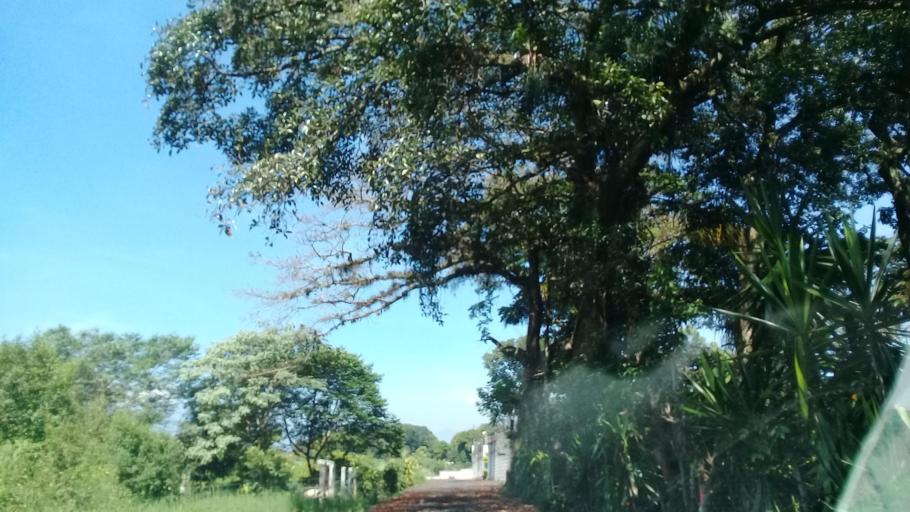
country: MX
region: Veracruz
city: Amatlan de los Reyes
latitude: 18.8543
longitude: -96.9223
